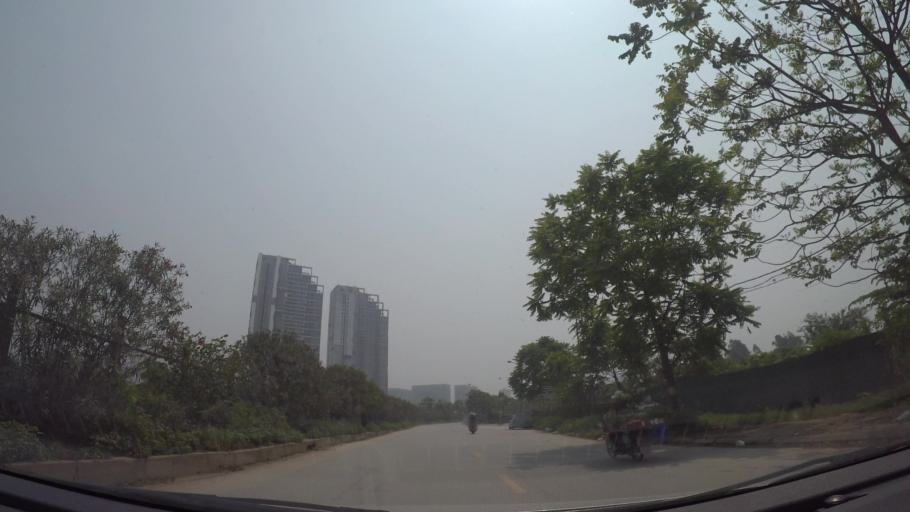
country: VN
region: Ha Noi
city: Cau Dien
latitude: 21.0047
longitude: 105.7663
